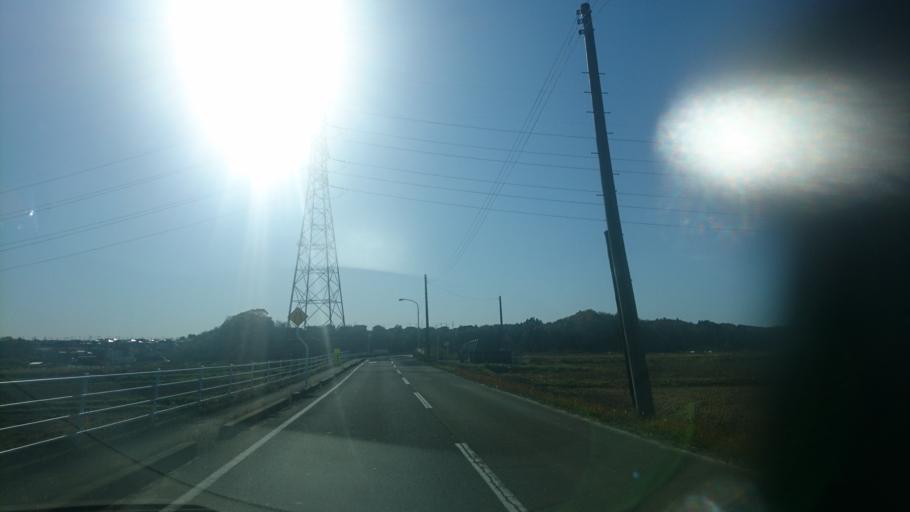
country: JP
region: Miyagi
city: Tomiya
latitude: 38.4134
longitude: 140.8795
